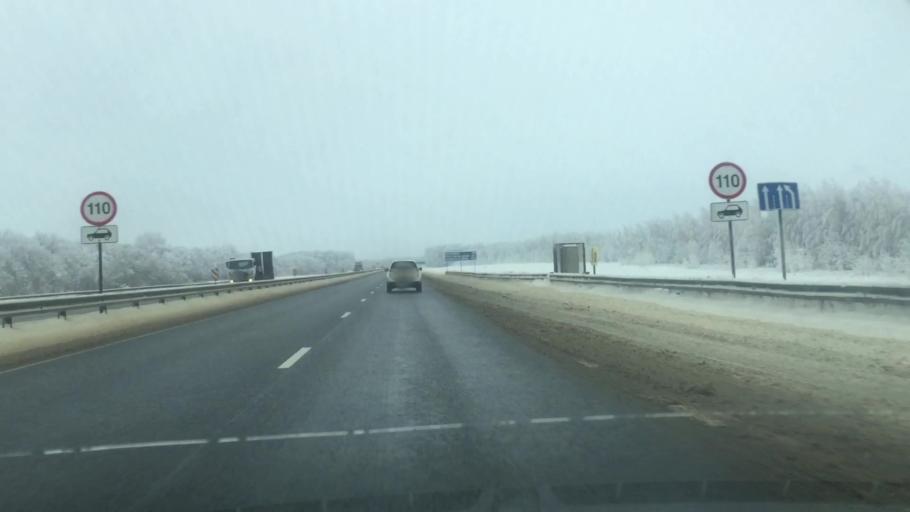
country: RU
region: Lipetsk
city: Zadonsk
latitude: 52.4997
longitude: 38.7553
